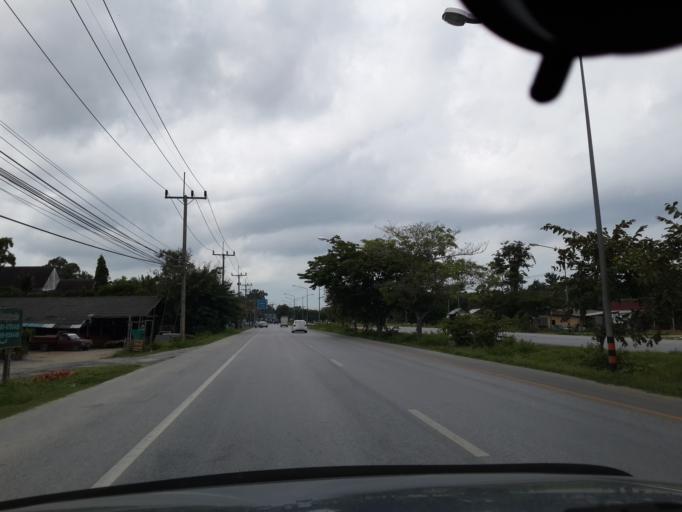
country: TH
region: Pattani
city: Pattani
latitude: 6.8726
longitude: 101.3070
